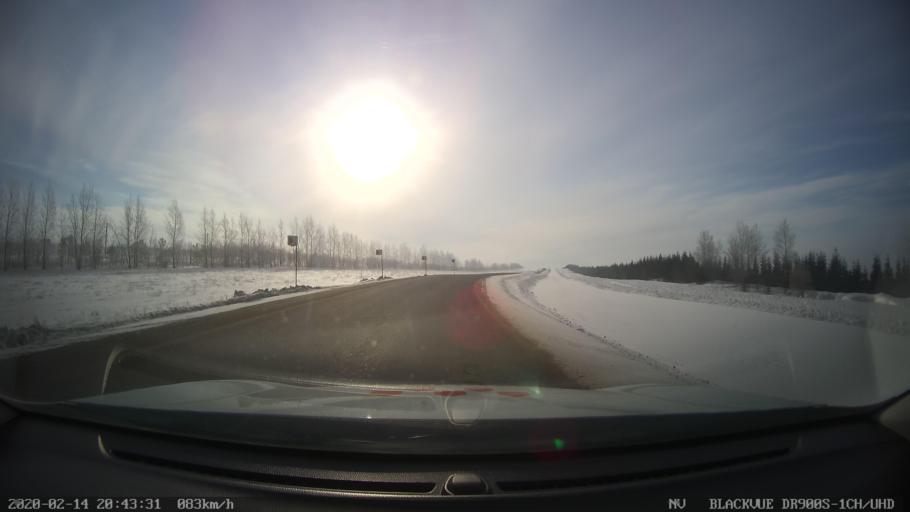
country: RU
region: Tatarstan
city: Kuybyshevskiy Zaton
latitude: 55.3071
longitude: 49.1483
